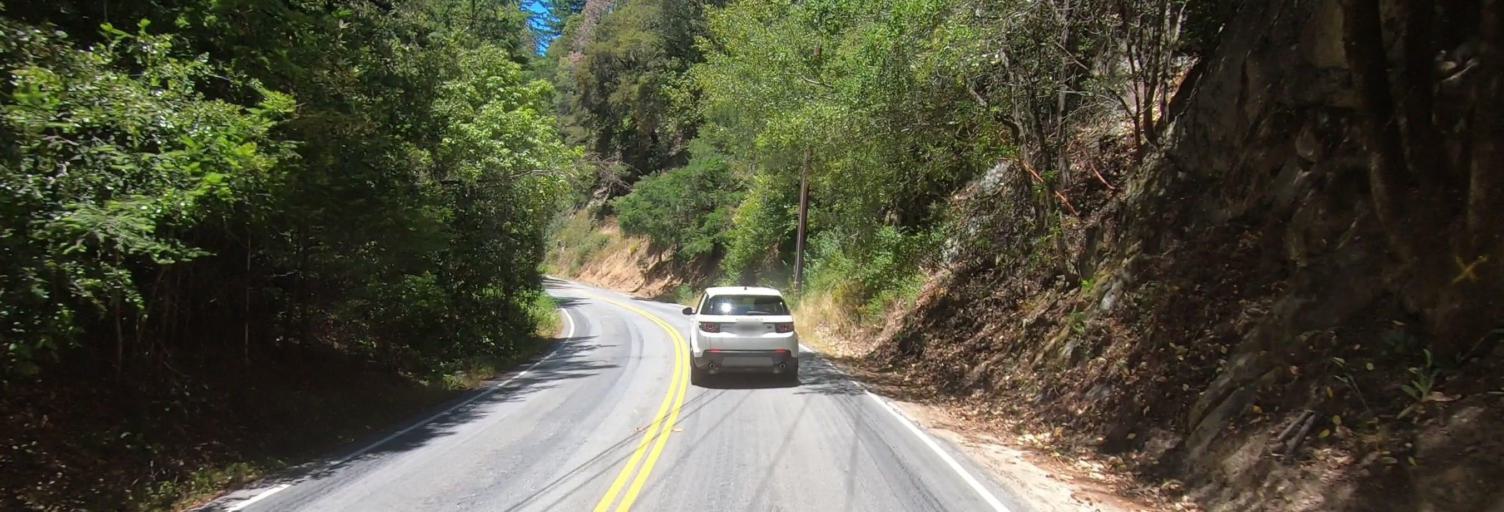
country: US
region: California
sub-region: San Mateo County
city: Woodside
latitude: 37.3942
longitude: -122.2869
